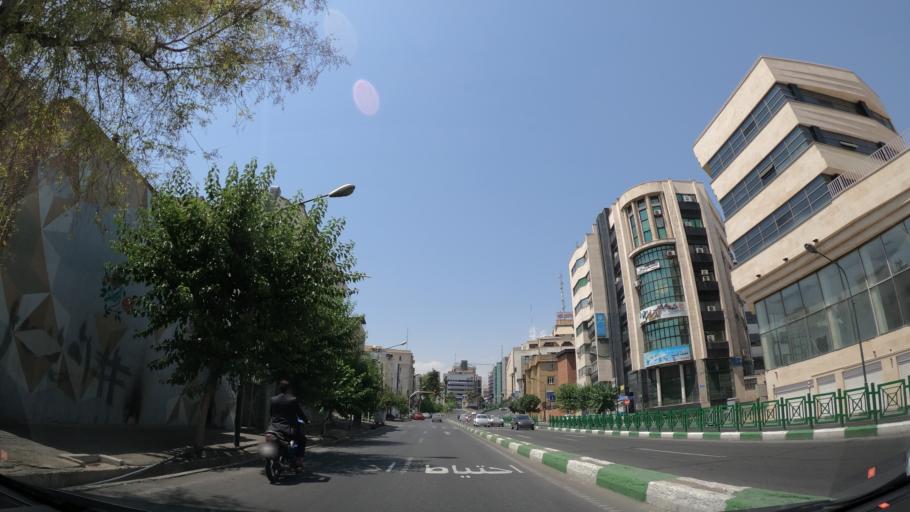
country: IR
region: Tehran
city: Tehran
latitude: 35.7270
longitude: 51.4146
